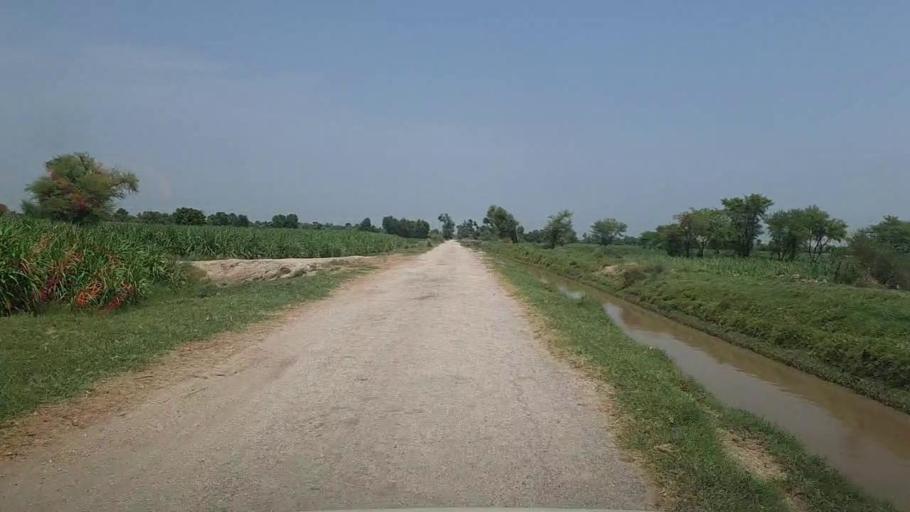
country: PK
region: Sindh
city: Karaundi
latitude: 26.8875
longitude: 68.3337
